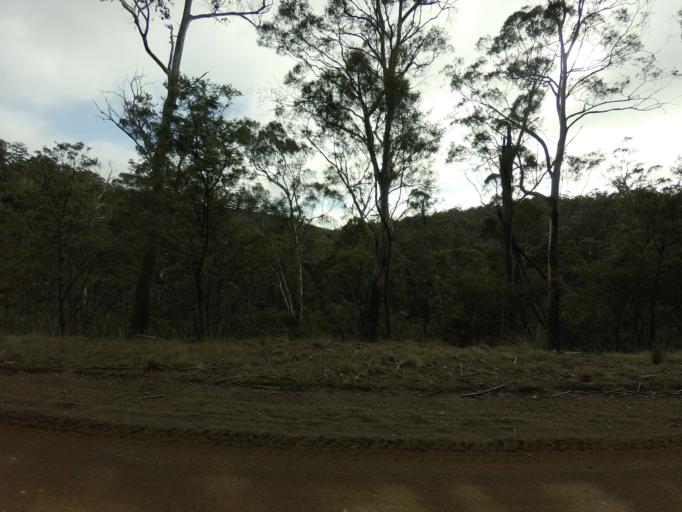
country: AU
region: Tasmania
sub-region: Derwent Valley
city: New Norfolk
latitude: -42.7506
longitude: 146.8718
